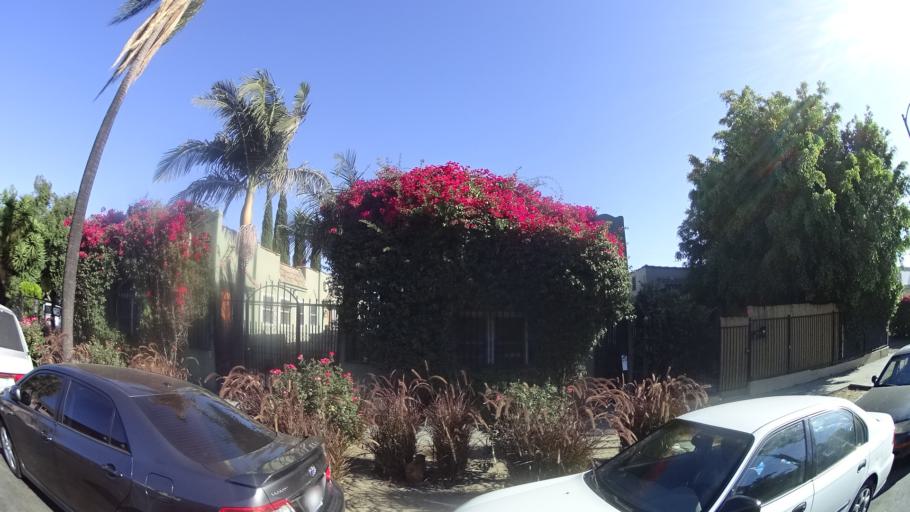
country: US
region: California
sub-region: Los Angeles County
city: Hollywood
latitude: 34.0889
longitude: -118.3256
